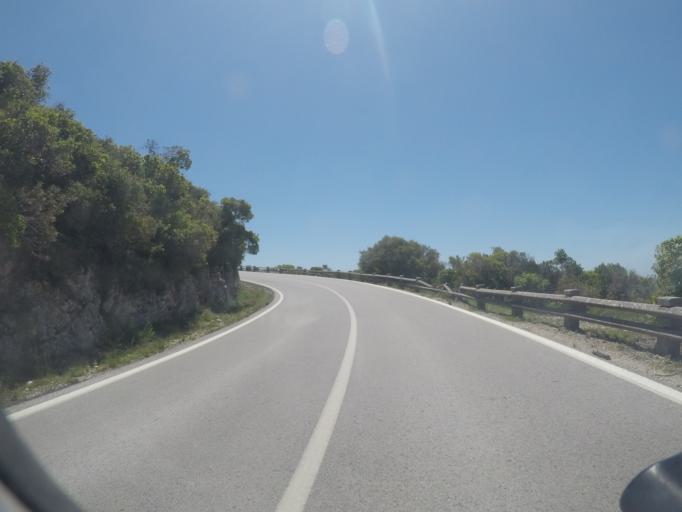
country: PT
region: Setubal
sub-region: Sesimbra
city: Sesimbra
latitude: 38.4604
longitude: -9.0161
